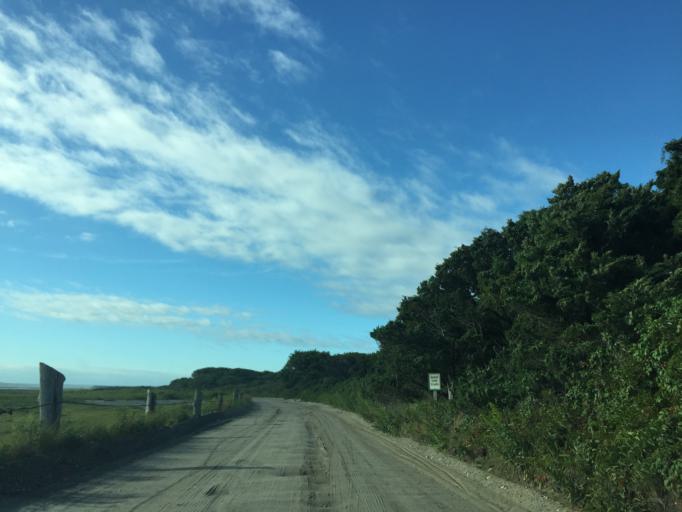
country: US
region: Massachusetts
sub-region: Plymouth County
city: Duxbury
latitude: 42.0145
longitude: -70.6117
